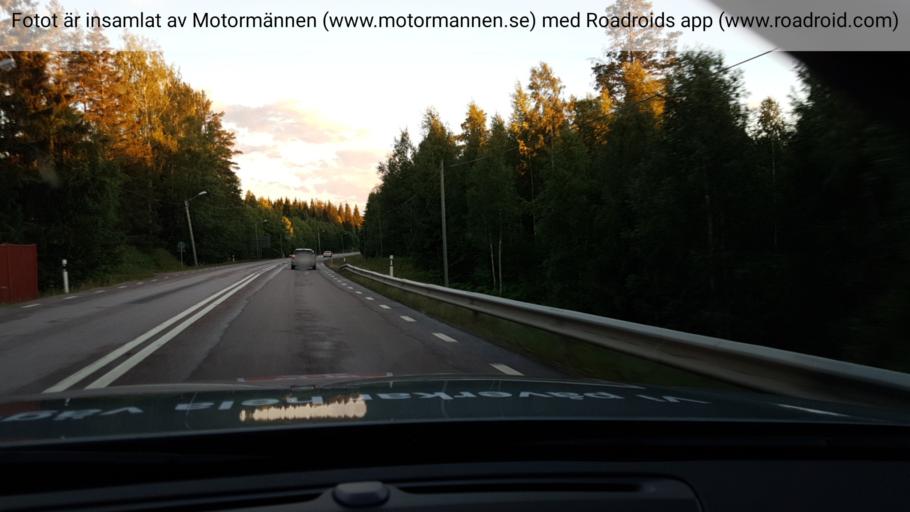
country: SE
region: Vaestmanland
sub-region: Fagersta Kommun
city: Fagersta
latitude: 59.9620
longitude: 15.7633
